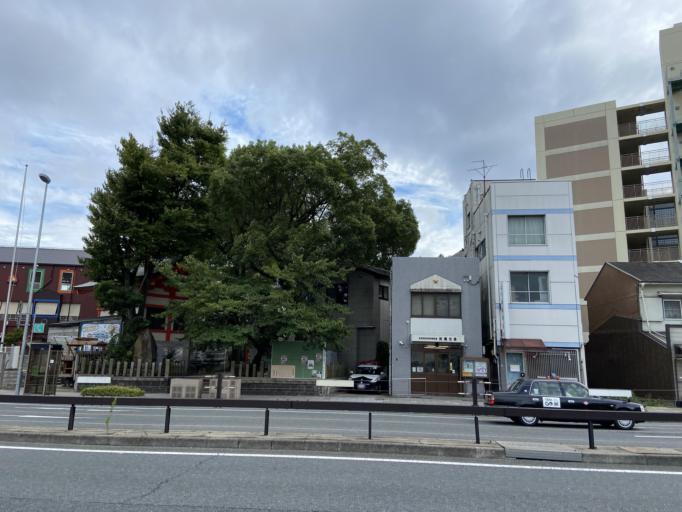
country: JP
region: Hyogo
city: Amagasaki
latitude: 34.7198
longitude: 135.4393
